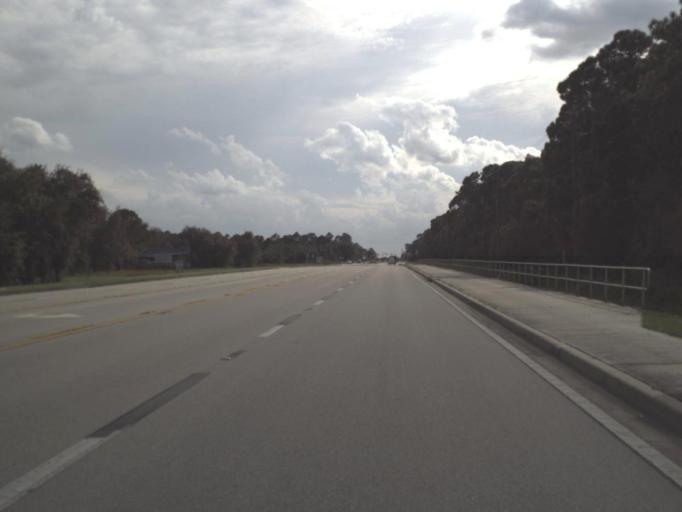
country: US
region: Florida
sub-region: Hendry County
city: LaBelle
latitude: 26.7532
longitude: -81.4565
